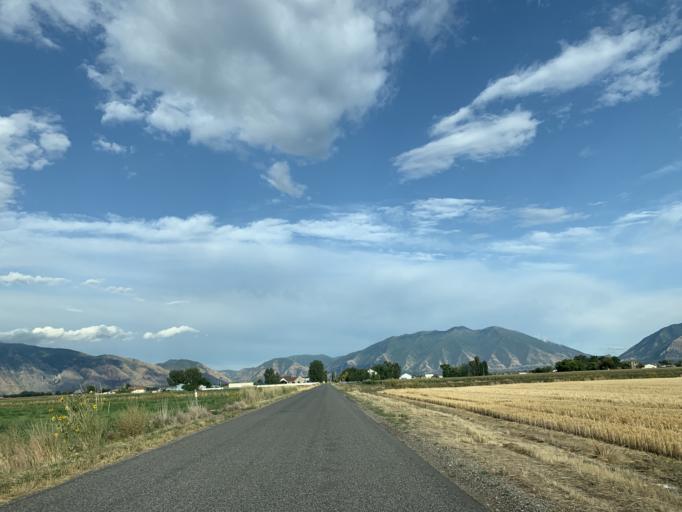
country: US
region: Utah
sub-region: Utah County
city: Benjamin
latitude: 40.1292
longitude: -111.7365
